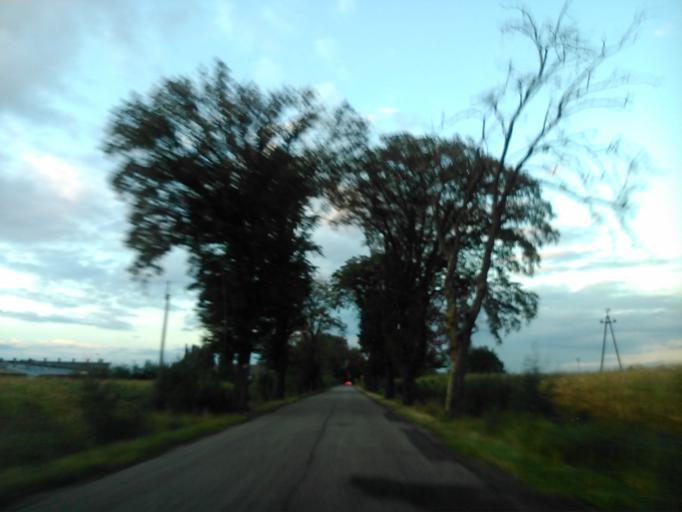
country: PL
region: Kujawsko-Pomorskie
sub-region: Powiat wabrzeski
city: Debowa Laka
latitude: 53.2008
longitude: 19.1640
